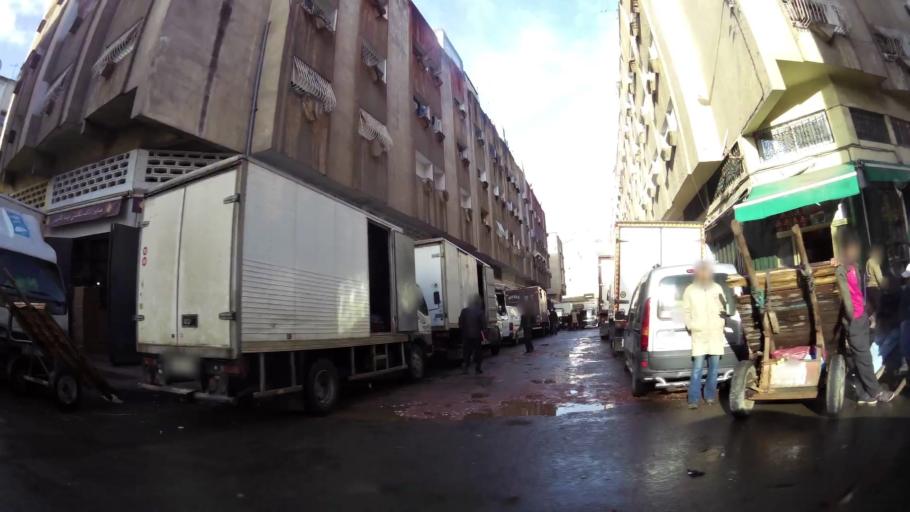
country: MA
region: Grand Casablanca
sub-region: Casablanca
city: Casablanca
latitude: 33.5871
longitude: -7.6093
